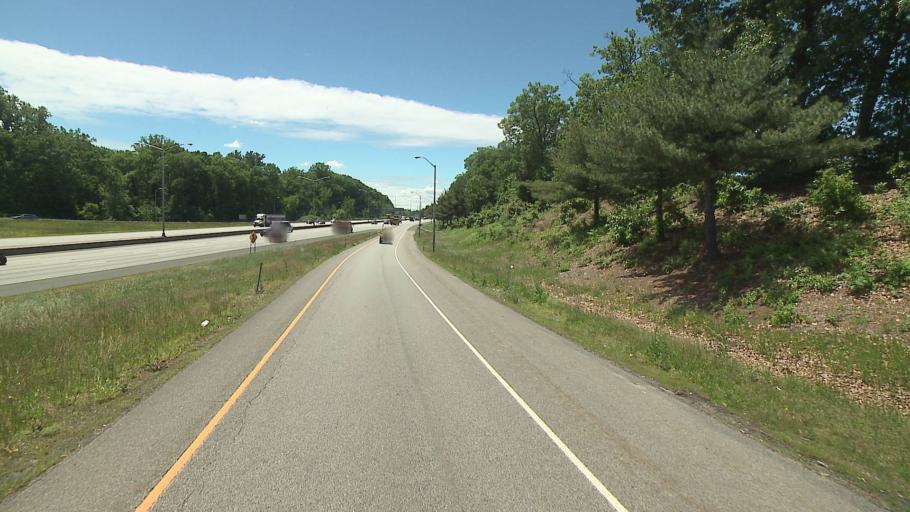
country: US
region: Connecticut
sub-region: Hartford County
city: Windsor
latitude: 41.8907
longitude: -72.6501
